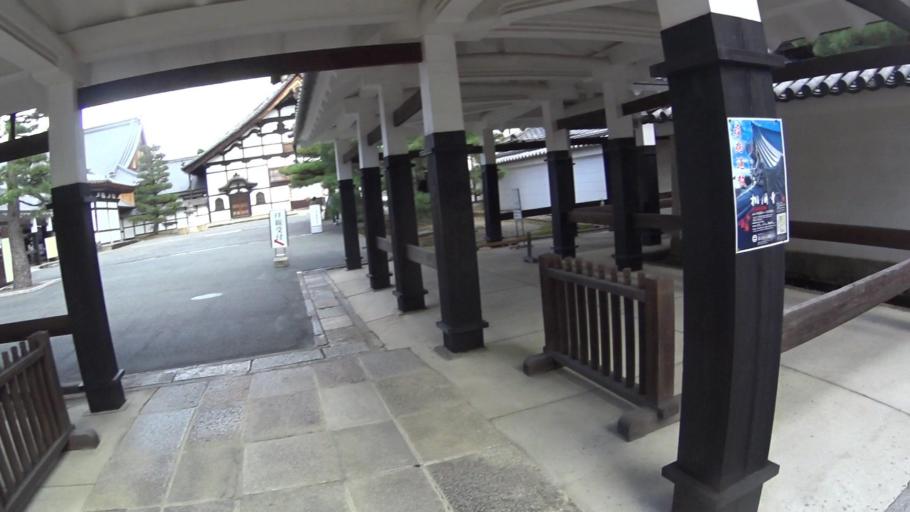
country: JP
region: Kyoto
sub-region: Kyoto-shi
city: Kamigyo-ku
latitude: 35.0343
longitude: 135.7608
